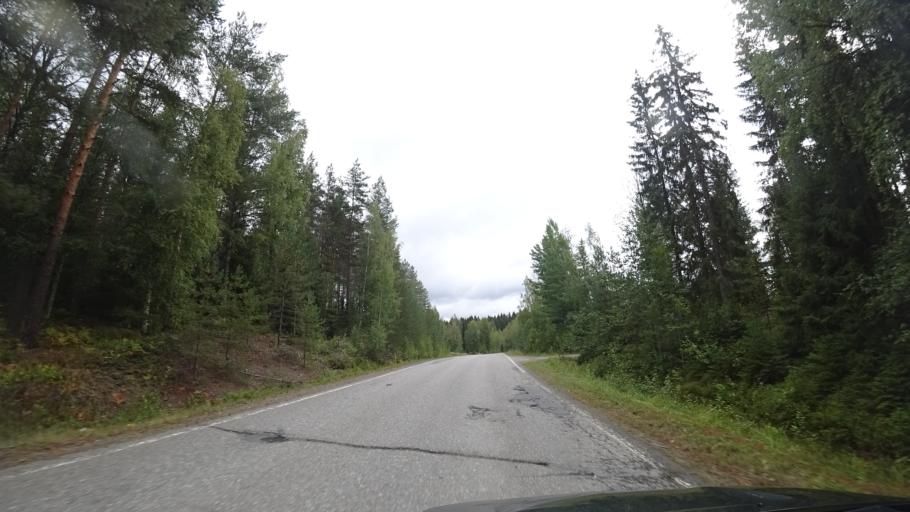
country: FI
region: Haeme
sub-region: Haemeenlinna
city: Lammi
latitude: 60.9951
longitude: 25.0276
